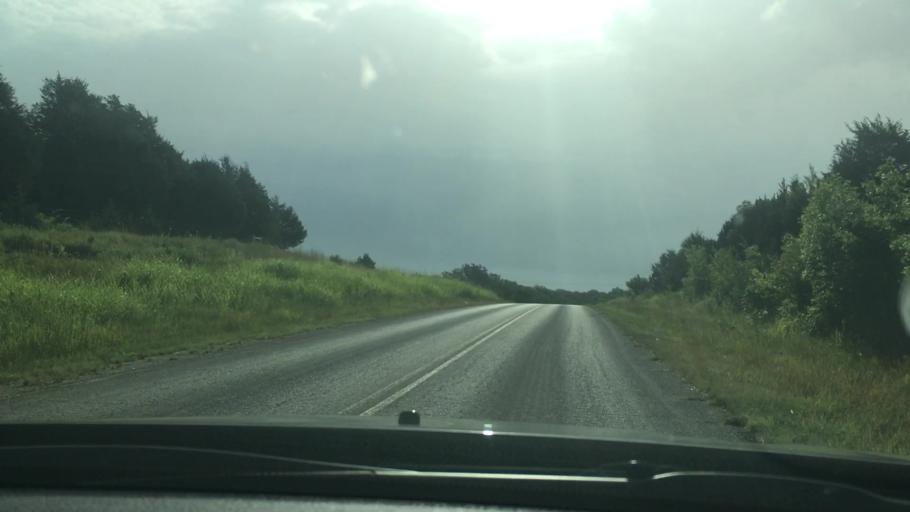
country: US
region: Oklahoma
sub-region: Pontotoc County
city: Byng
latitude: 34.8737
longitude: -96.5810
